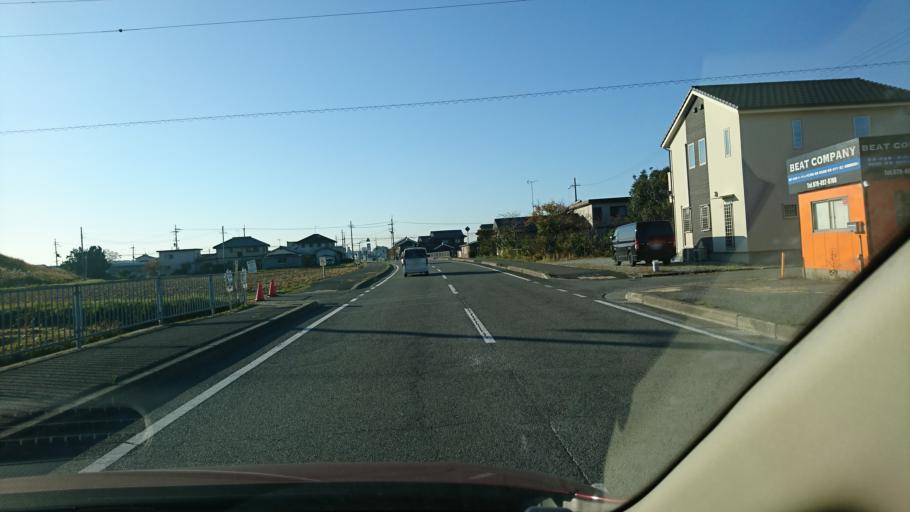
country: JP
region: Hyogo
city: Miki
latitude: 34.7640
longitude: 134.9197
